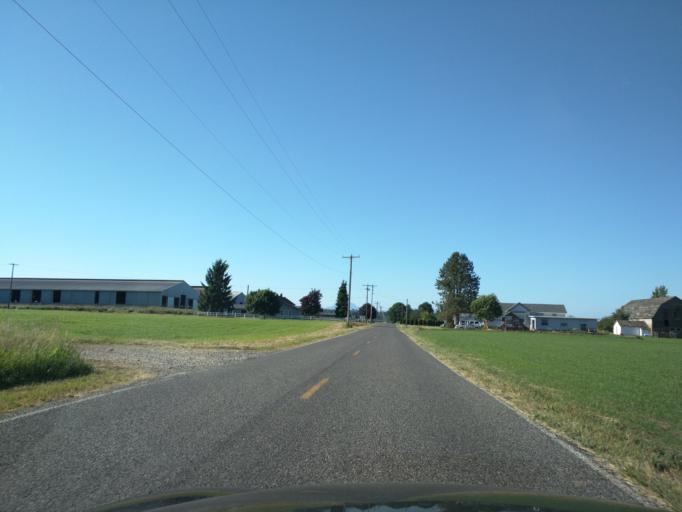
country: US
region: Washington
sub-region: Whatcom County
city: Lynden
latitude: 48.9815
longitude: -122.4518
